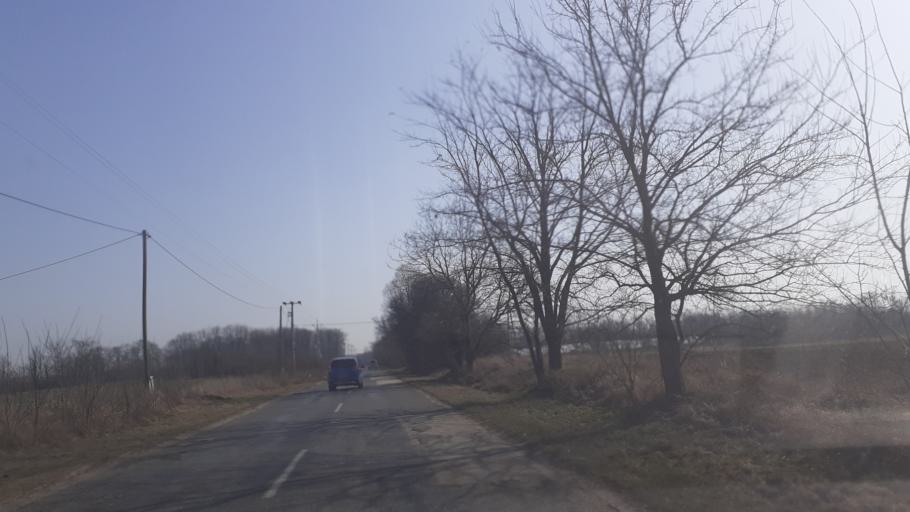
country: HU
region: Pest
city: Taborfalva
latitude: 47.0226
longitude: 19.4753
